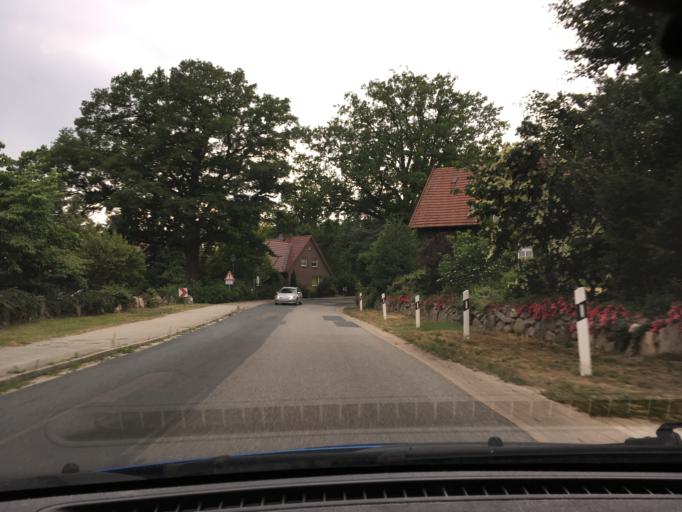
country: DE
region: Lower Saxony
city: Drestedt
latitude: 53.3268
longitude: 9.7753
